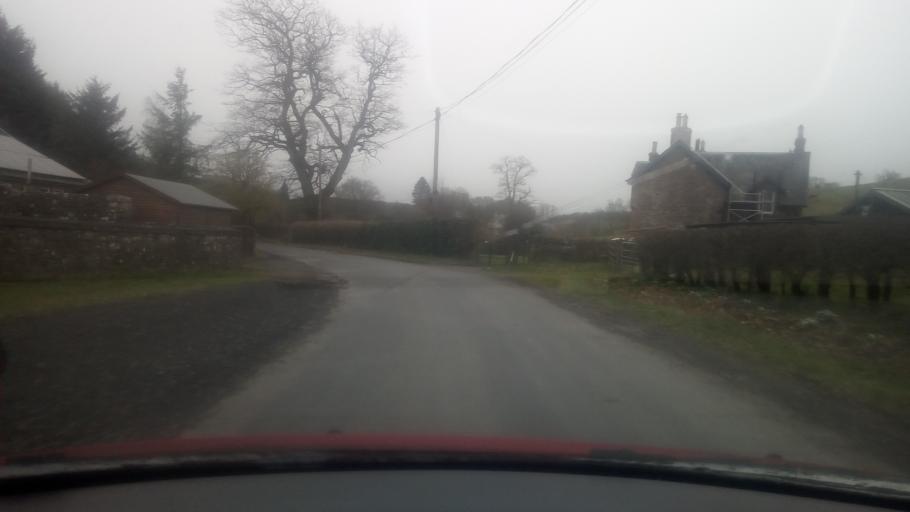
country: GB
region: Scotland
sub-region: The Scottish Borders
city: Jedburgh
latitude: 55.3904
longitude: -2.6541
